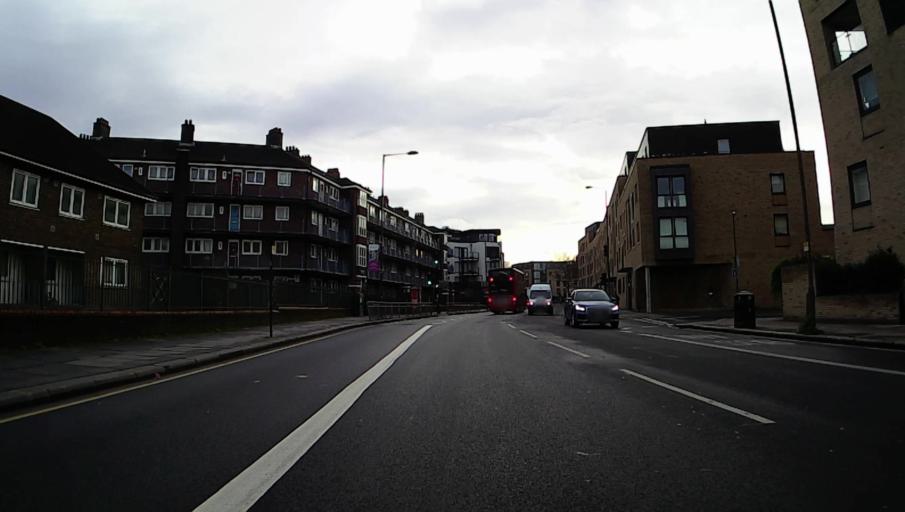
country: GB
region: England
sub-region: Greater London
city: Blackheath
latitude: 51.4875
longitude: 0.0076
